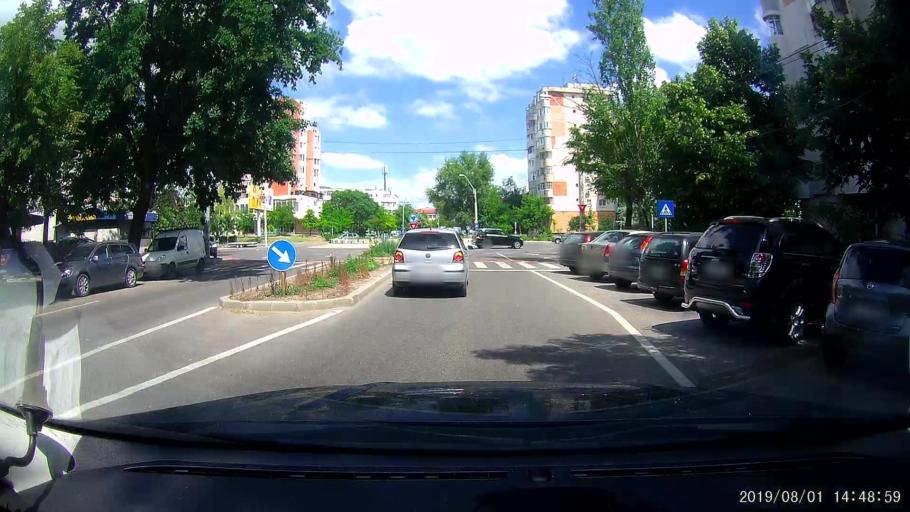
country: RO
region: Galati
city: Galati
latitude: 45.4093
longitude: 28.0143
